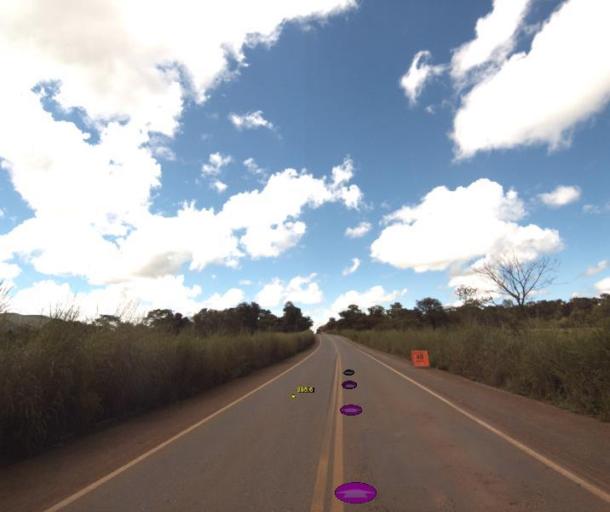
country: BR
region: Goias
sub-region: Petrolina De Goias
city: Petrolina de Goias
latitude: -16.0025
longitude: -49.1375
